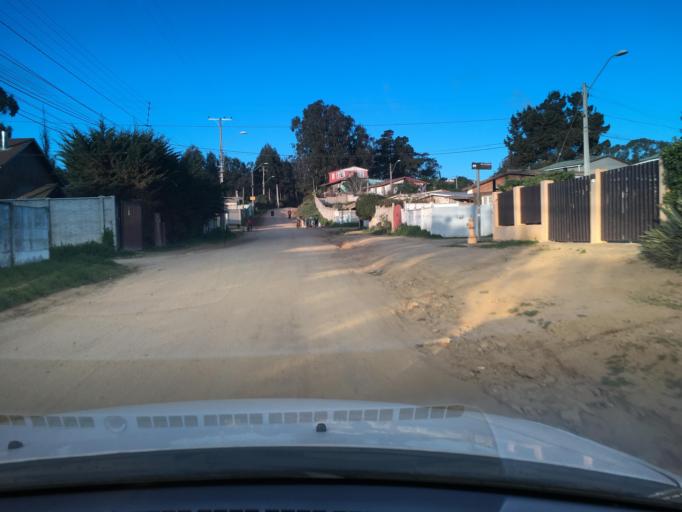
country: CL
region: Valparaiso
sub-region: San Antonio Province
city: El Tabo
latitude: -33.4540
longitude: -71.6565
